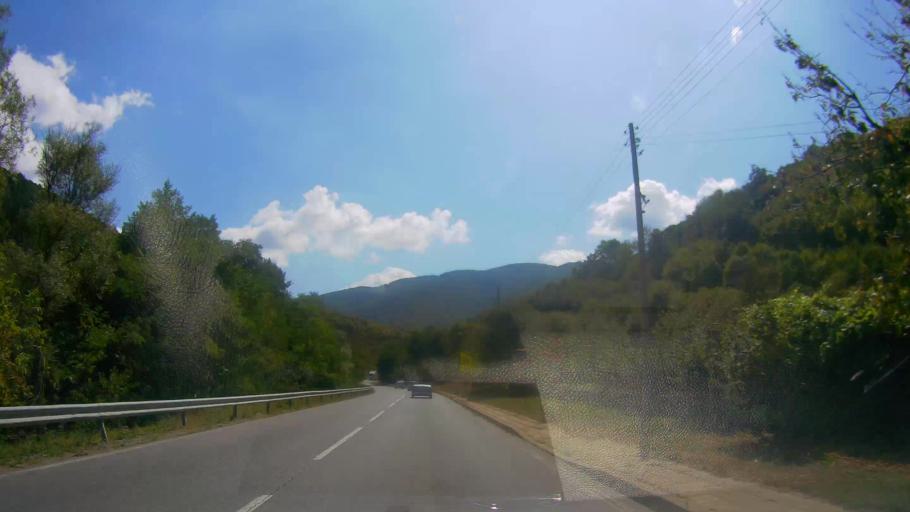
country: BG
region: Stara Zagora
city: Gurkovo
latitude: 42.7175
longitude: 25.7166
